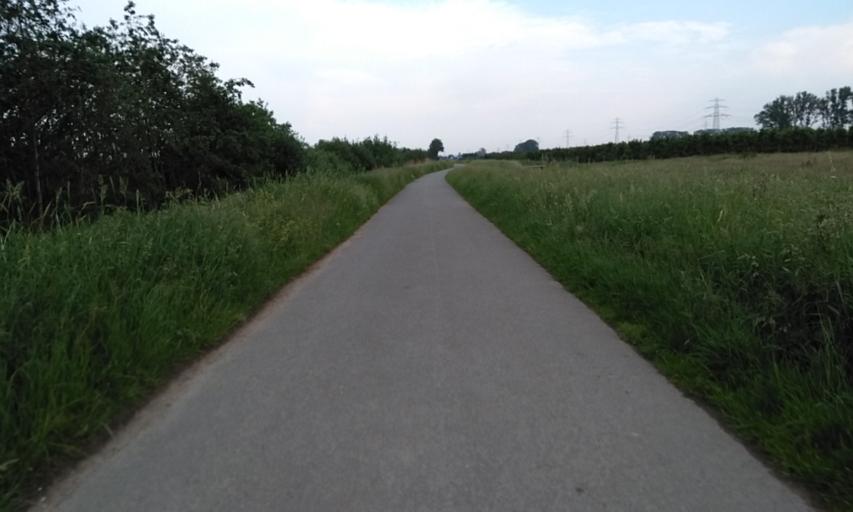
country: DE
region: Lower Saxony
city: Neuenkirchen
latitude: 53.5083
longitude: 9.6347
